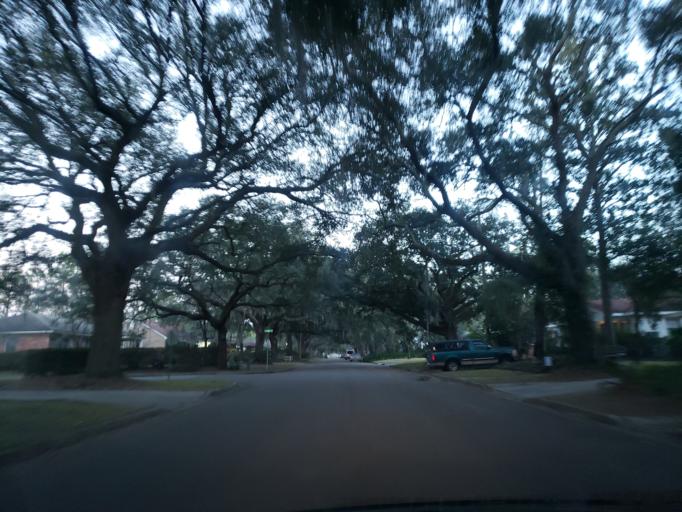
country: US
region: Georgia
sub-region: Chatham County
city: Thunderbolt
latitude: 32.0179
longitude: -81.0822
